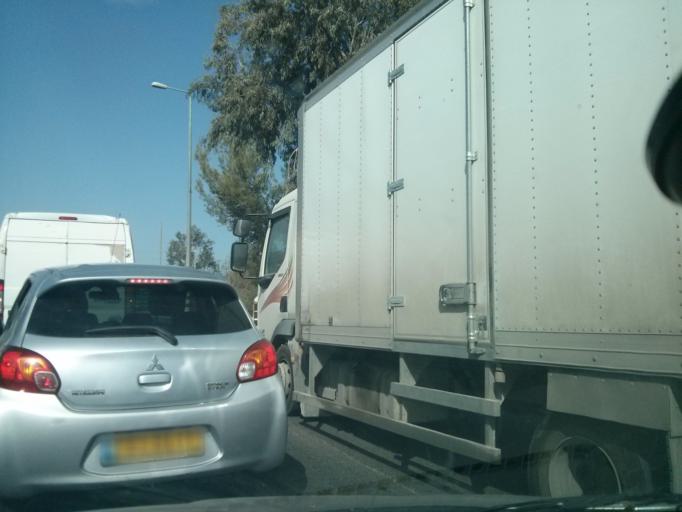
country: IL
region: Jerusalem
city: Bet Shemesh
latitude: 31.7612
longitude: 34.9922
